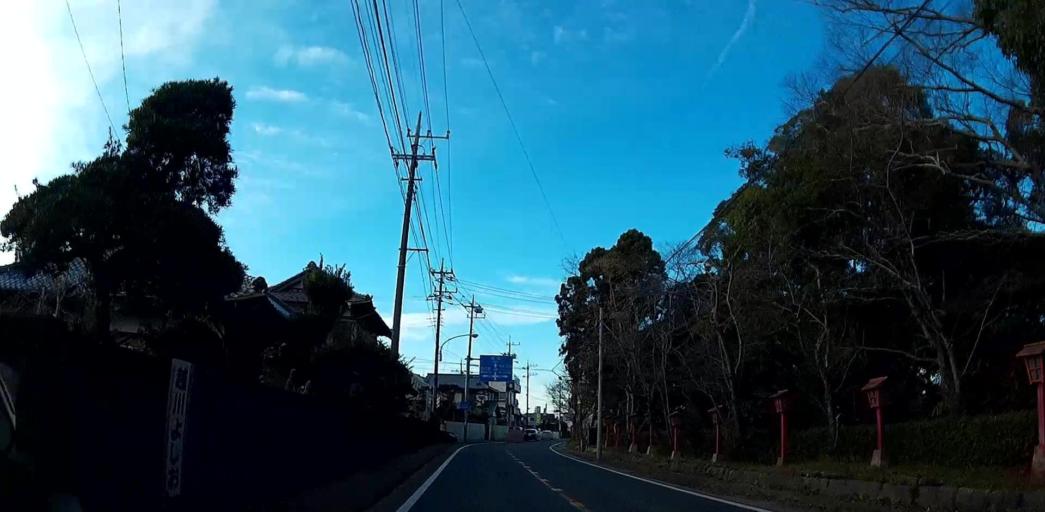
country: JP
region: Chiba
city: Omigawa
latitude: 35.8414
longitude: 140.6590
